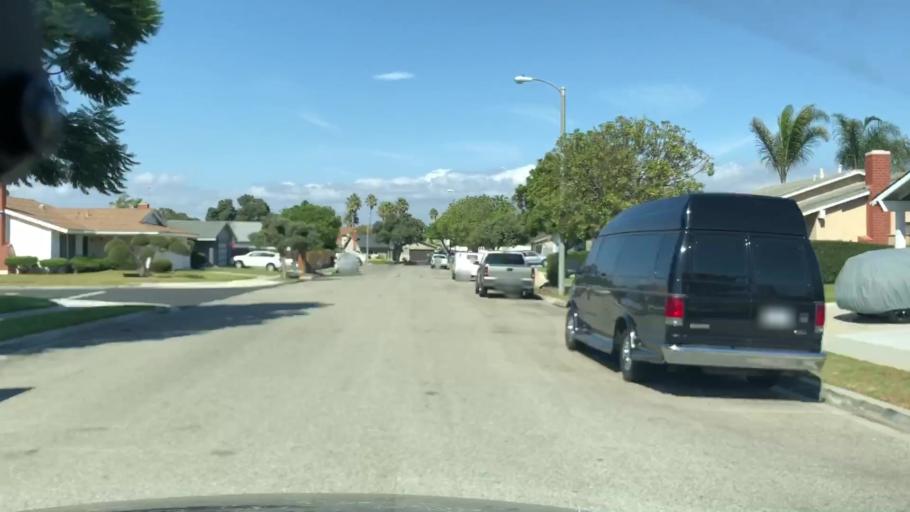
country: US
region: California
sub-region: Ventura County
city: Oxnard Shores
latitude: 34.1873
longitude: -119.2163
